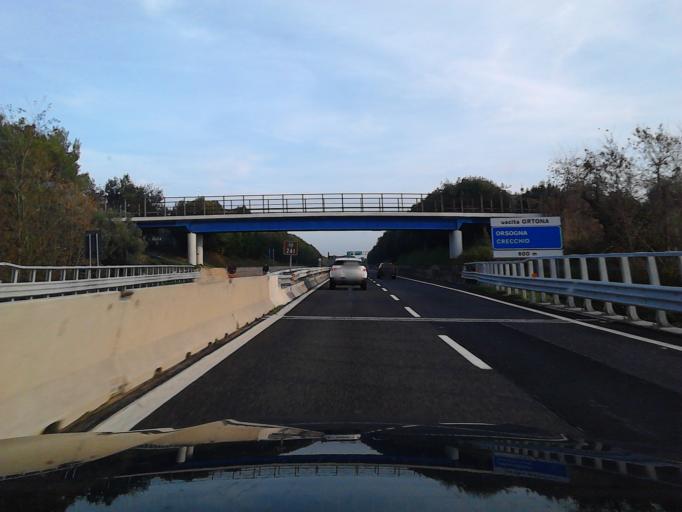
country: IT
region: Abruzzo
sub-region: Provincia di Chieti
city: Ortona
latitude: 42.3333
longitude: 14.3736
